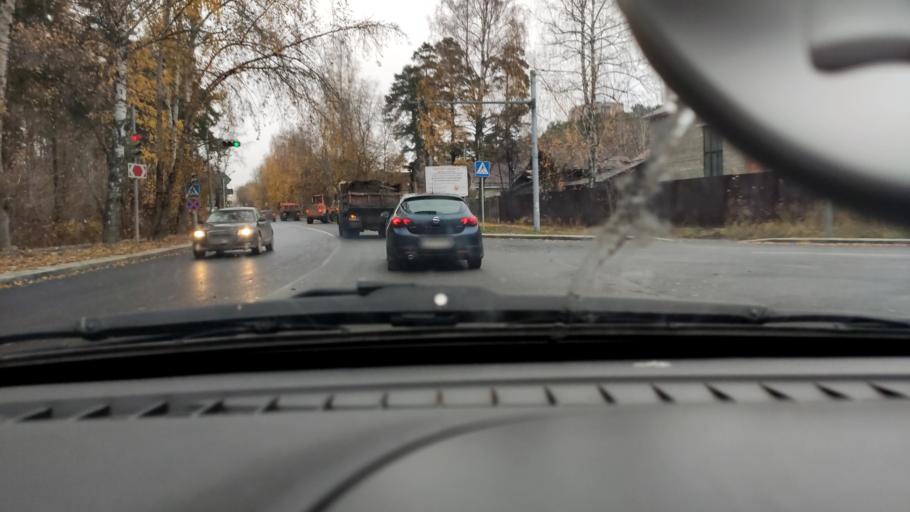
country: RU
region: Perm
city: Kondratovo
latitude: 58.0210
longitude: 56.0117
